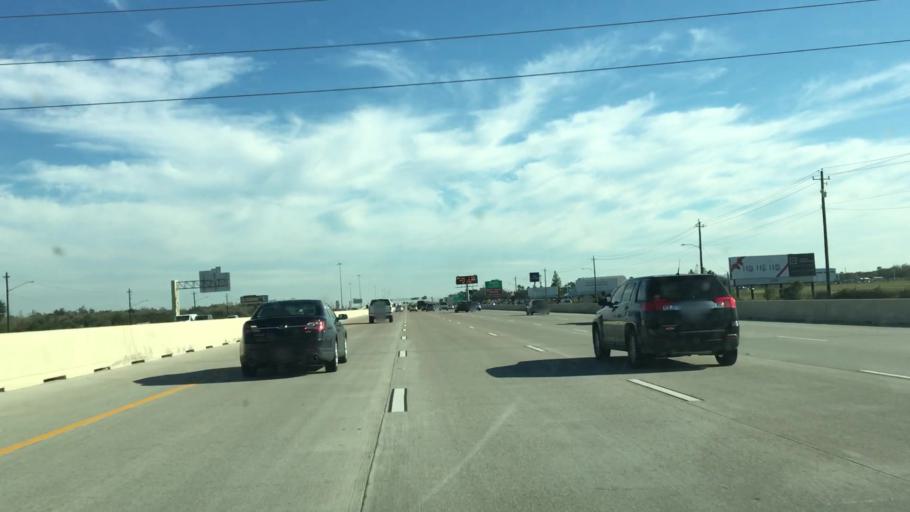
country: US
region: Texas
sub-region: Harris County
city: Webster
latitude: 29.5614
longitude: -95.1618
